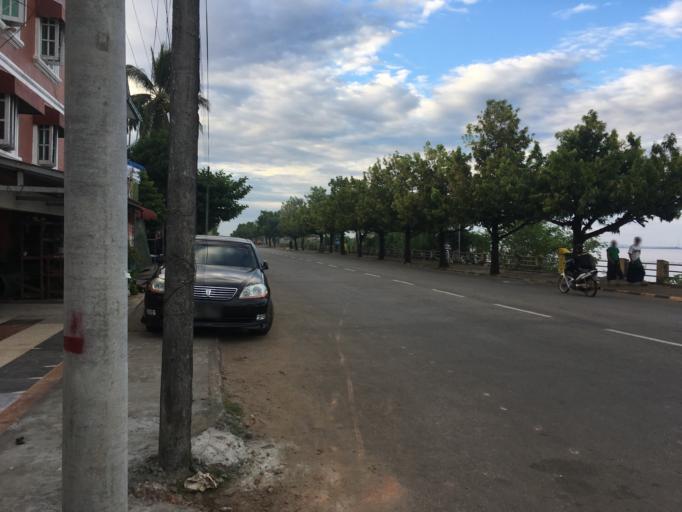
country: MM
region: Mon
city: Mawlamyine
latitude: 16.4756
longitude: 97.6200
